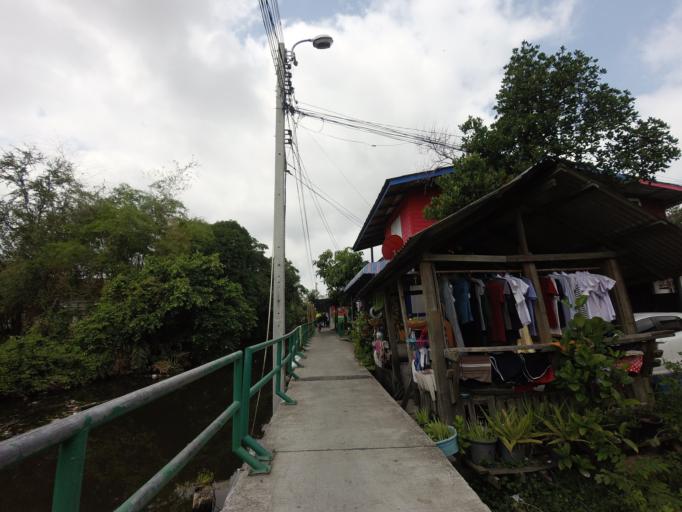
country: TH
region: Bangkok
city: Thung Khru
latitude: 13.6449
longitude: 100.5068
